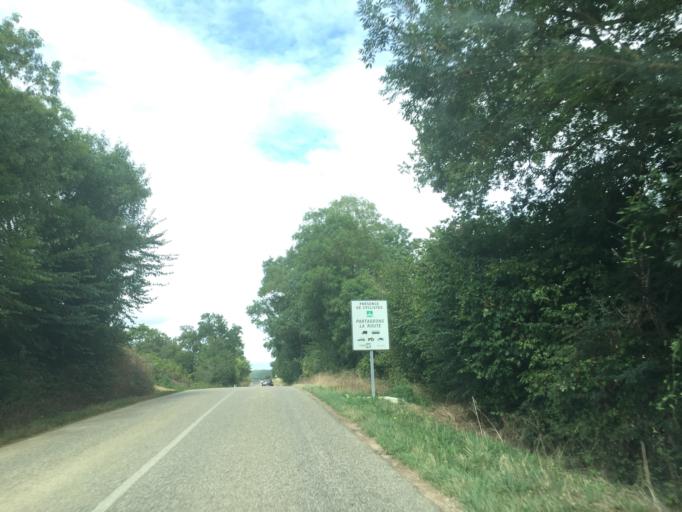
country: FR
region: Midi-Pyrenees
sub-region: Departement du Gers
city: Jegun
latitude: 43.6749
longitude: 0.3915
